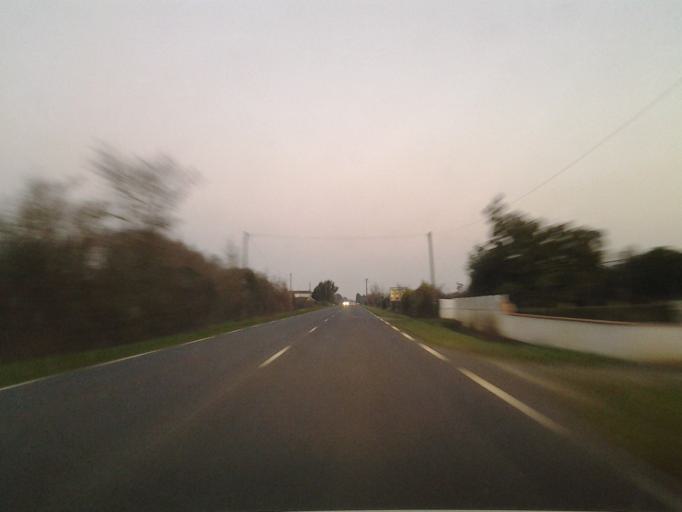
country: FR
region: Pays de la Loire
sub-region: Departement de la Vendee
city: Sallertaine
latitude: 46.8805
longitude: -1.9590
